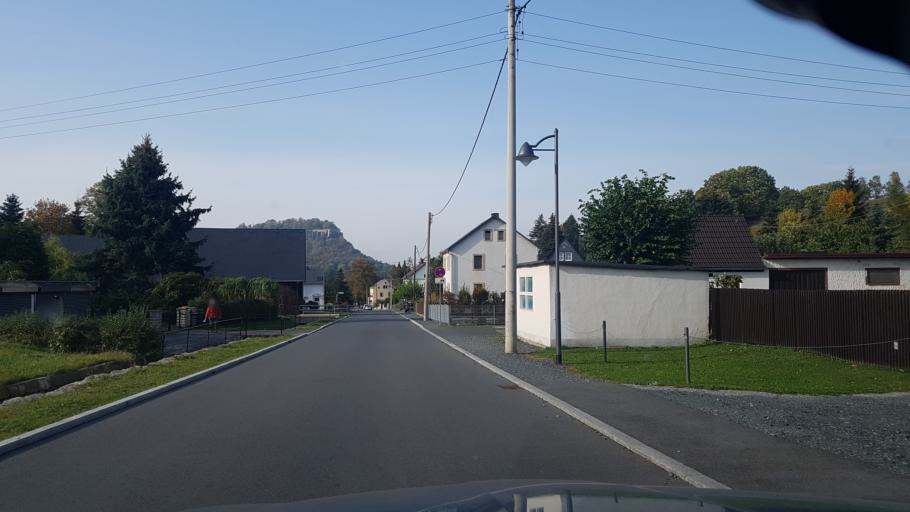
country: DE
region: Saxony
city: Konigstein
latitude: 50.9085
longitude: 14.0793
